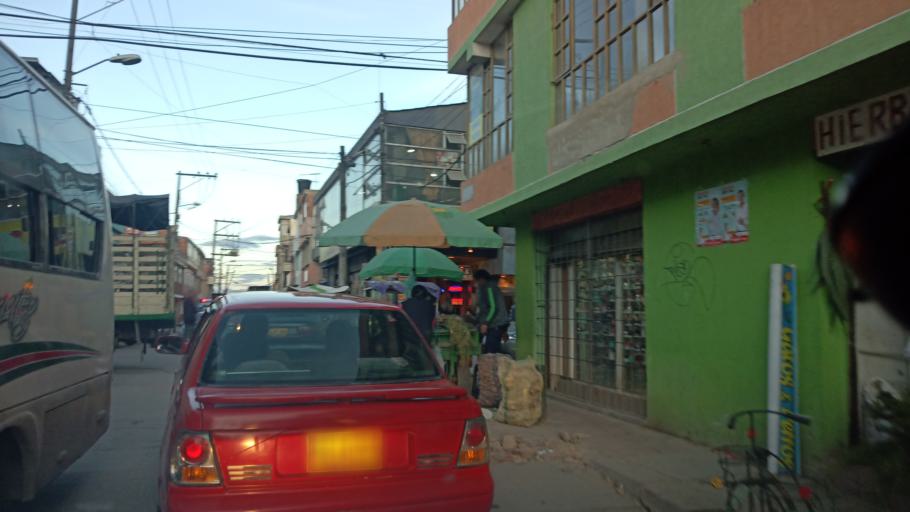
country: CO
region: Cundinamarca
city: Soacha
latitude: 4.5787
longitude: -74.2161
